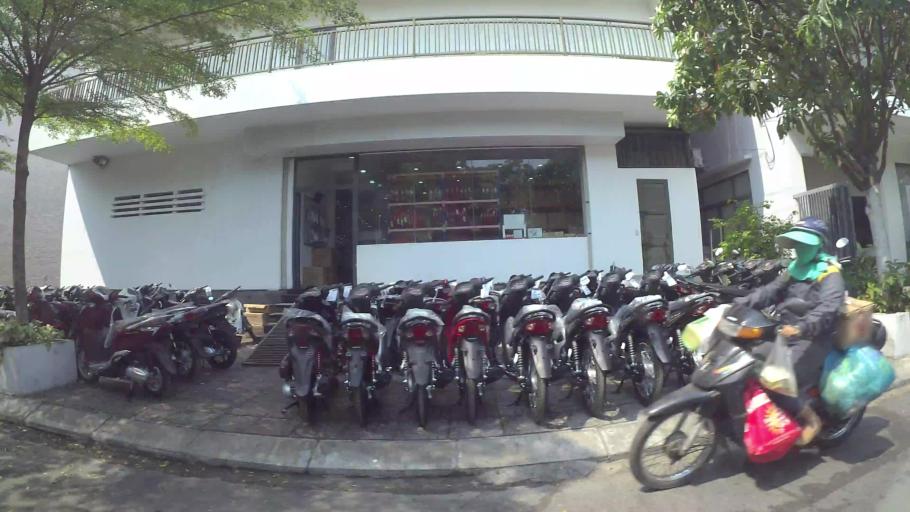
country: VN
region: Da Nang
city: Son Tra
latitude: 16.0390
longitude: 108.2433
